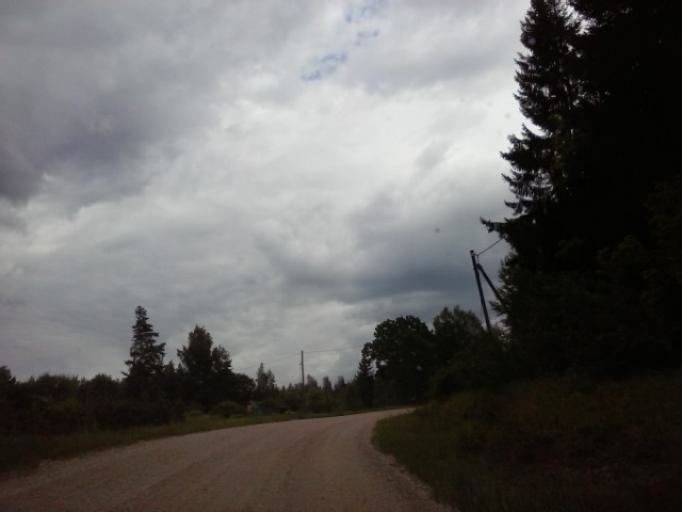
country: EE
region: Vorumaa
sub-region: Voru linn
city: Voru
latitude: 57.7445
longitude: 27.0851
